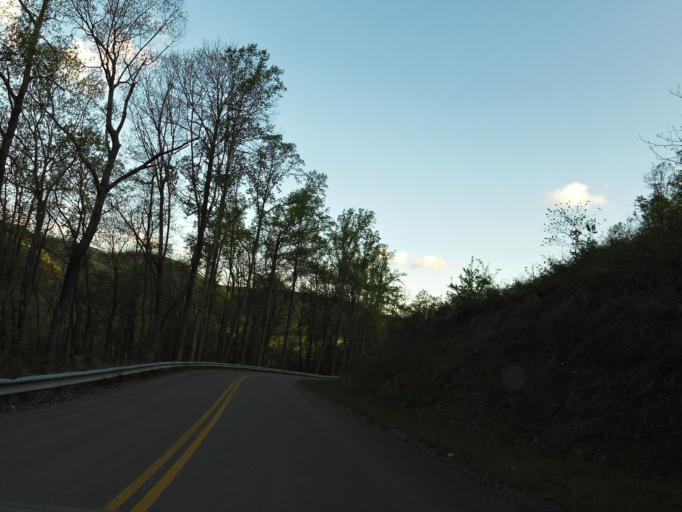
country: US
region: Kentucky
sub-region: Bell County
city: Middlesboro
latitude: 36.6183
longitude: -83.8788
